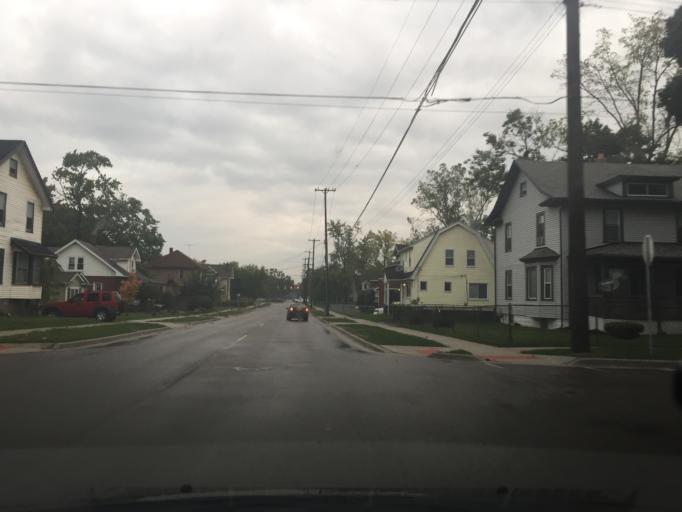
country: US
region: Michigan
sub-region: Oakland County
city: Pontiac
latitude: 42.6324
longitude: -83.2822
